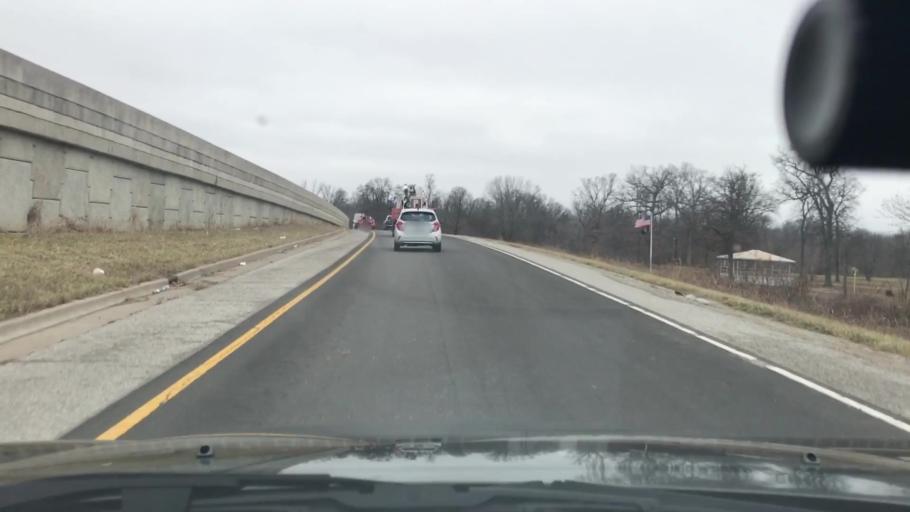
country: US
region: Illinois
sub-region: Madison County
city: Rosewood Heights
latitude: 38.9010
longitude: -90.0658
